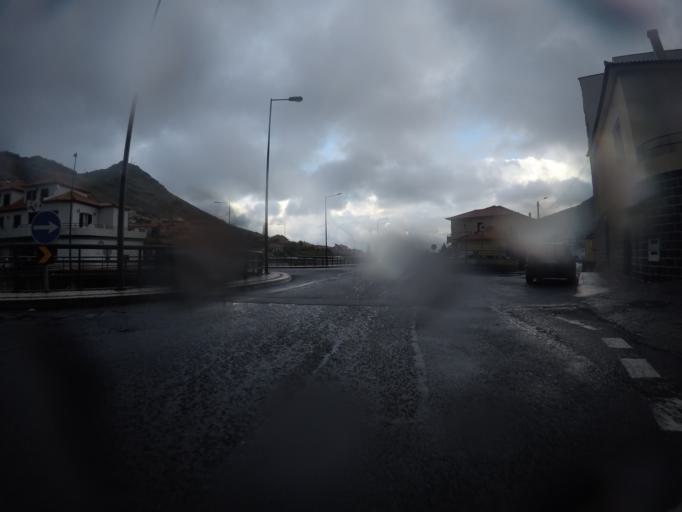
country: PT
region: Madeira
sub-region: Machico
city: Machico
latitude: 32.7240
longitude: -16.7705
